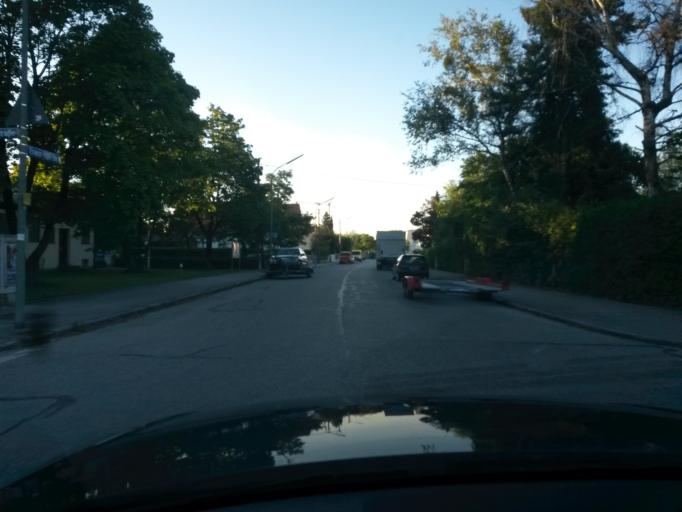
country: DE
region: Bavaria
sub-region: Upper Bavaria
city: Karlsfeld
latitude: 48.1942
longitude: 11.4617
